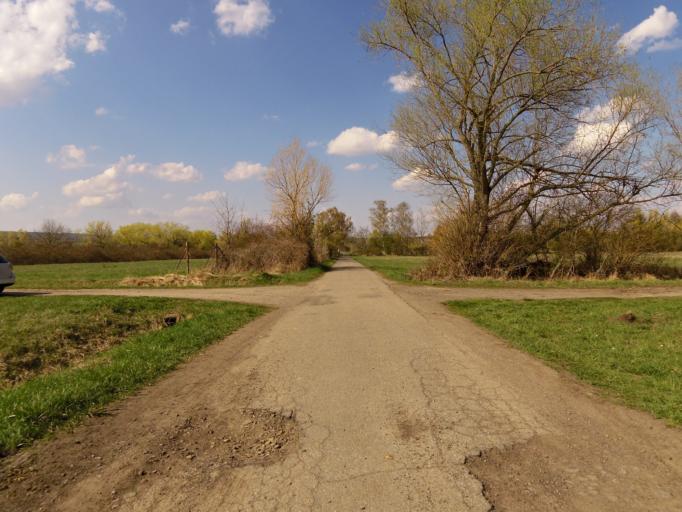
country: DE
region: Rheinland-Pfalz
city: Erpolzheim
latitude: 49.4819
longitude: 8.2035
